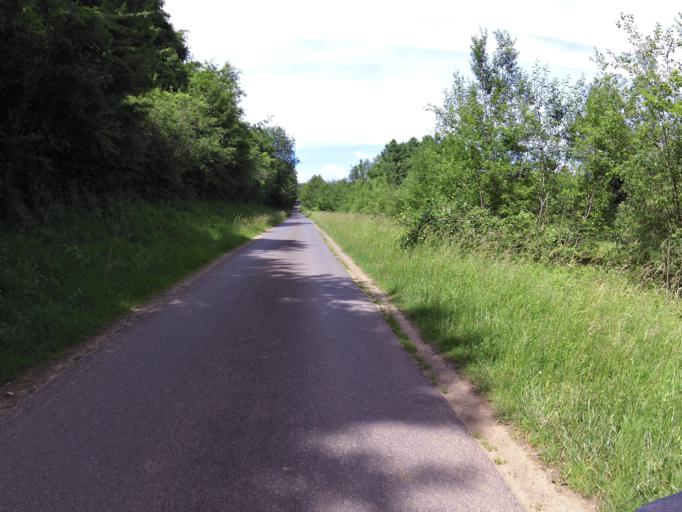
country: FR
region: Champagne-Ardenne
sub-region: Departement des Ardennes
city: Mouzon
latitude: 49.5390
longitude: 5.0860
